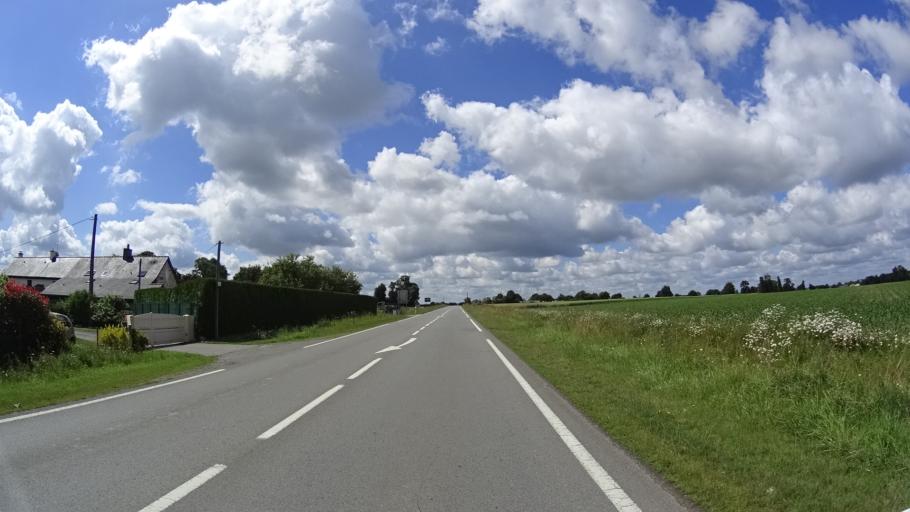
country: FR
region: Brittany
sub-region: Departement d'Ille-et-Vilaine
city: Le Rheu
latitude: 48.1129
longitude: -1.8259
